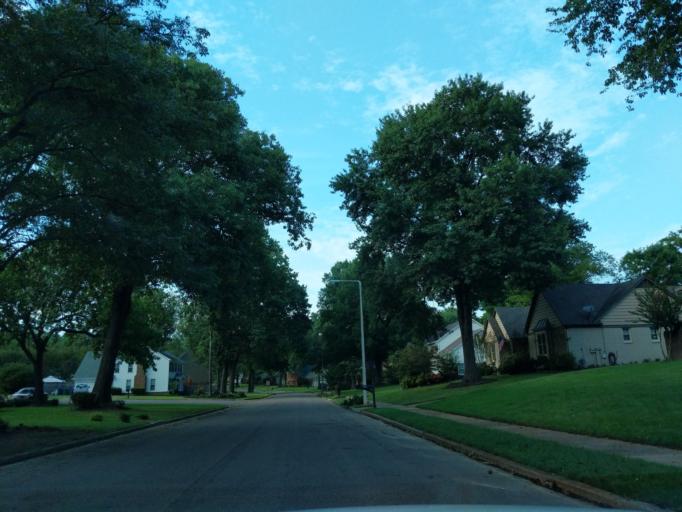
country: US
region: Tennessee
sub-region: Shelby County
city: Germantown
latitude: 35.0649
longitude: -89.7845
